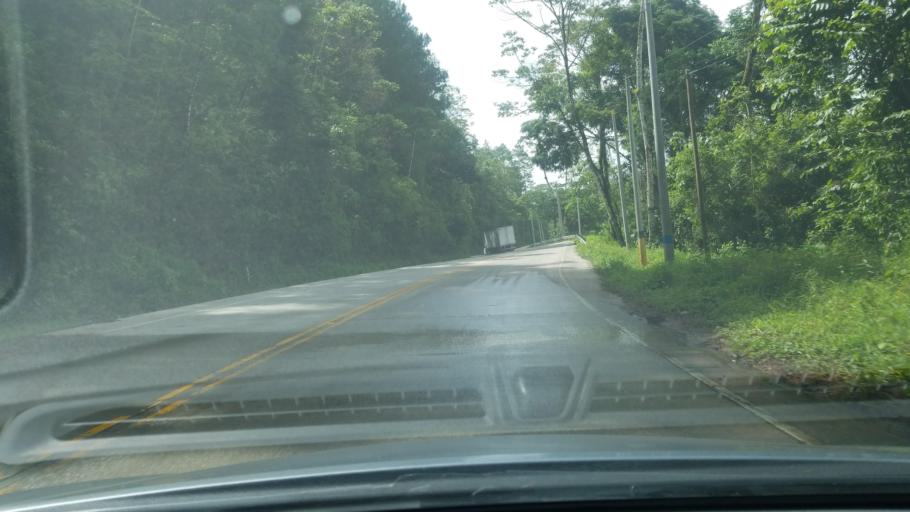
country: HN
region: Copan
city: San Jeronimo
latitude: 14.9317
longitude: -88.9422
